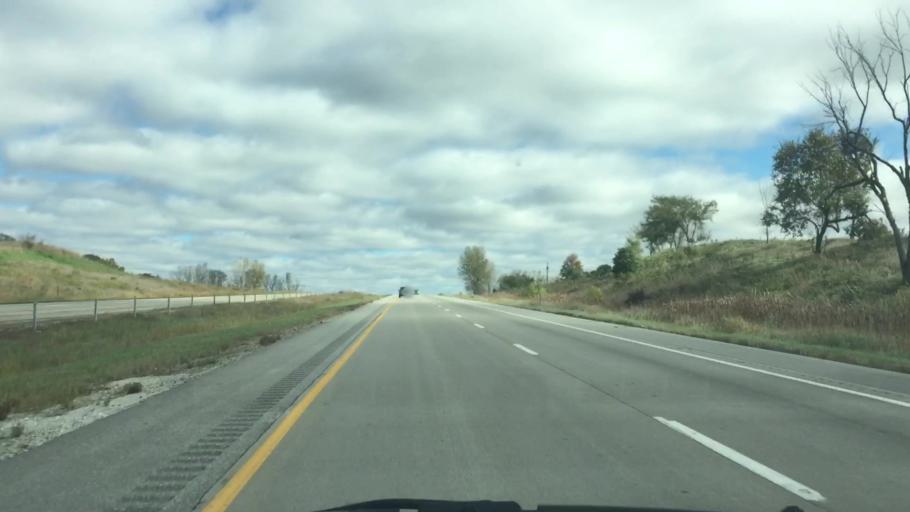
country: US
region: Iowa
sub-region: Jasper County
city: Newton
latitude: 41.6815
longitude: -93.0910
